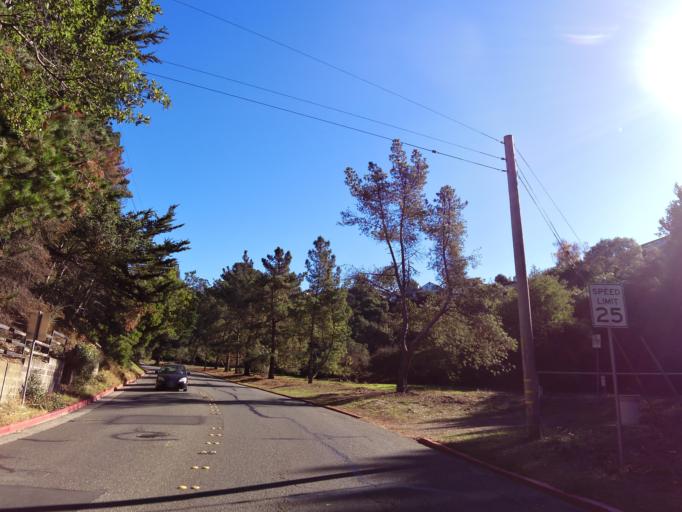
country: US
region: California
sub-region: Alameda County
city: Piedmont
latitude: 37.8300
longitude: -122.2281
